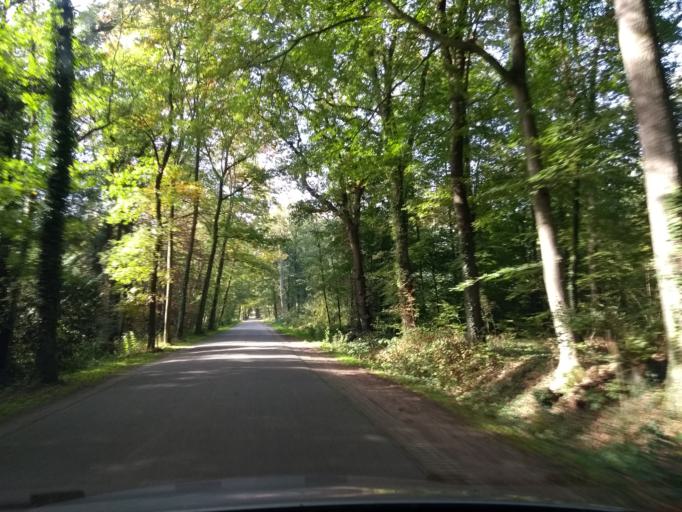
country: NL
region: Gelderland
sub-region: Gemeente Lochem
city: Barchem
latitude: 52.1009
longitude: 6.3931
